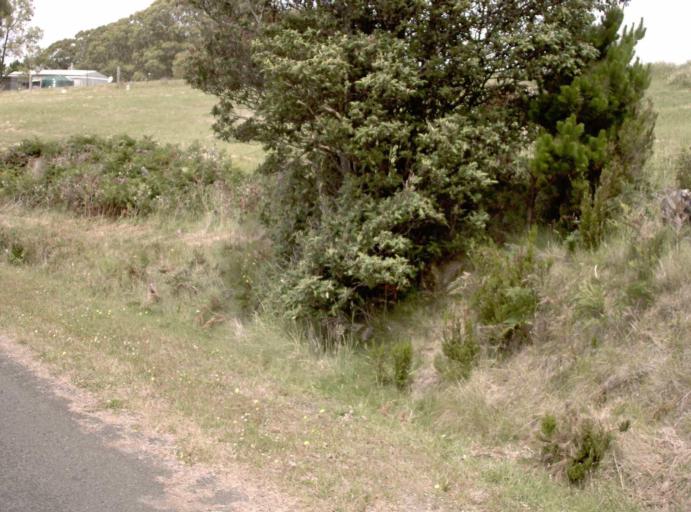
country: AU
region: Victoria
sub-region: Latrobe
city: Traralgon
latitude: -38.3713
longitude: 146.6899
